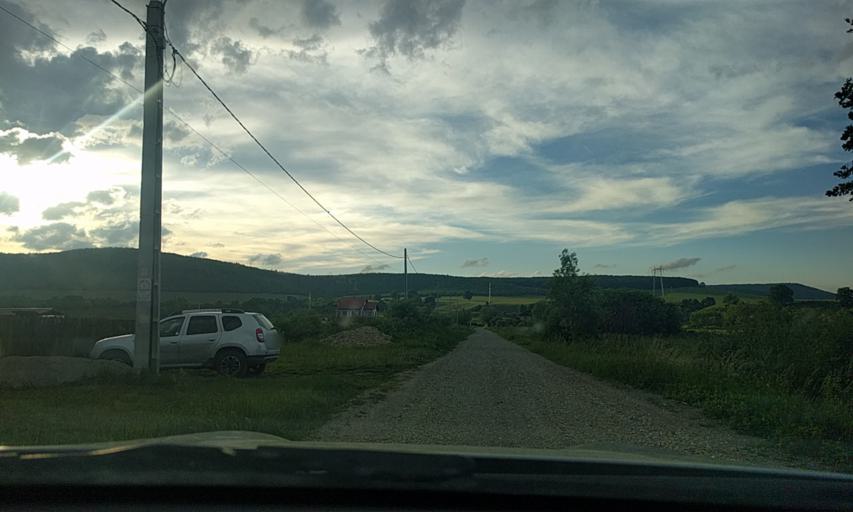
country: RO
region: Covasna
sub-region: Comuna Ilieni
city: Ilieni
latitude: 45.7652
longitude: 25.7183
